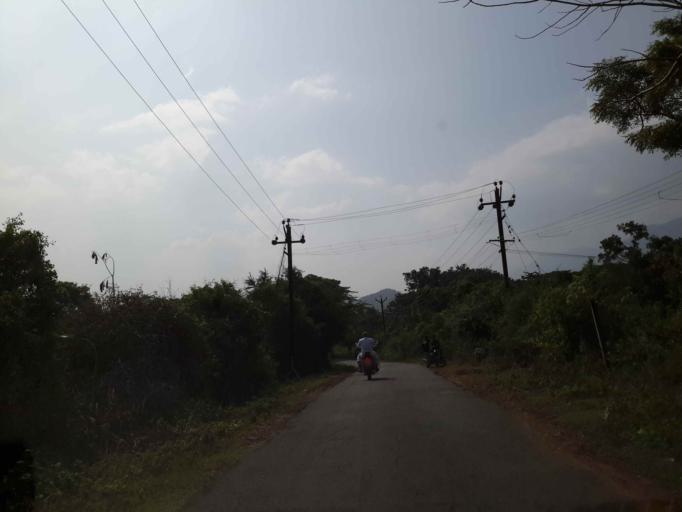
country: IN
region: Tamil Nadu
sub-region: Coimbatore
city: Mettupalayam
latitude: 11.2816
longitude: 76.8878
